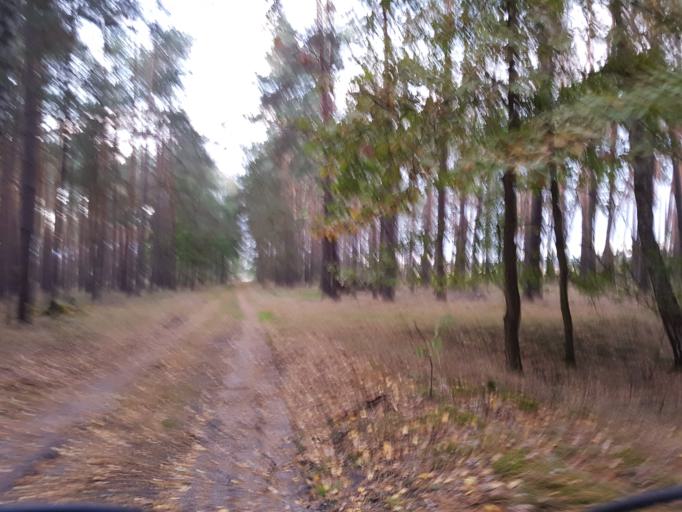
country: DE
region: Brandenburg
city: Schilda
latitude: 51.6049
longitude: 13.3642
